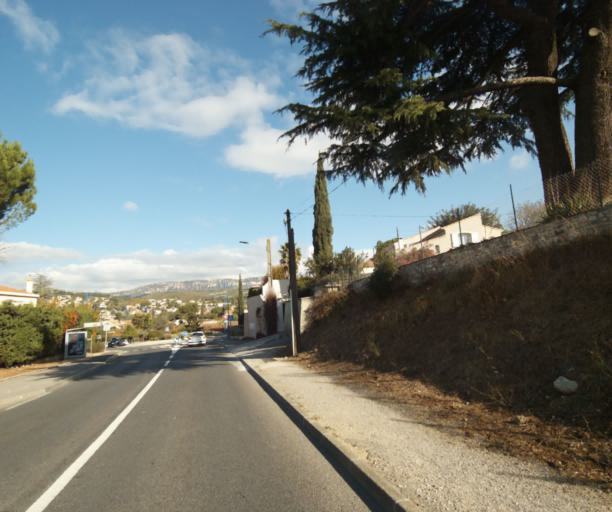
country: FR
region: Provence-Alpes-Cote d'Azur
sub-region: Departement des Bouches-du-Rhone
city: Allauch
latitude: 43.3527
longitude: 5.4877
